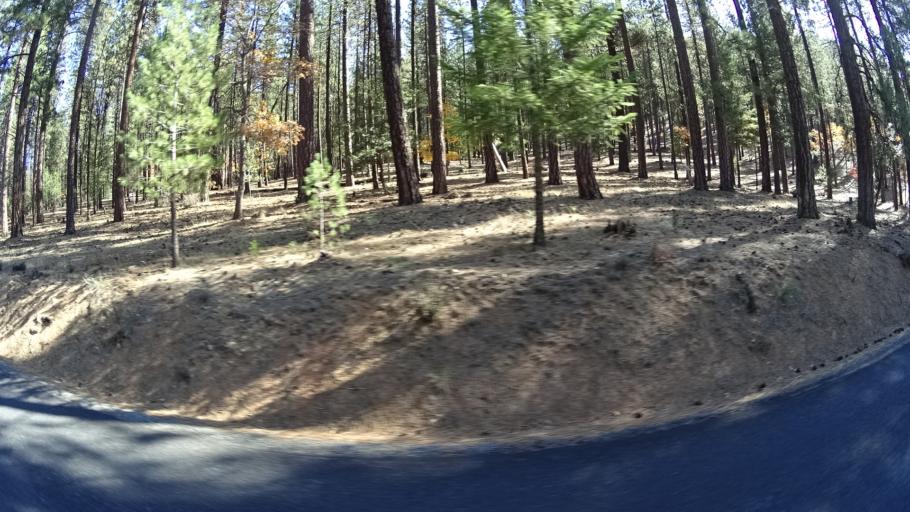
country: US
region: California
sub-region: Siskiyou County
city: Yreka
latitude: 41.6511
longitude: -122.8640
